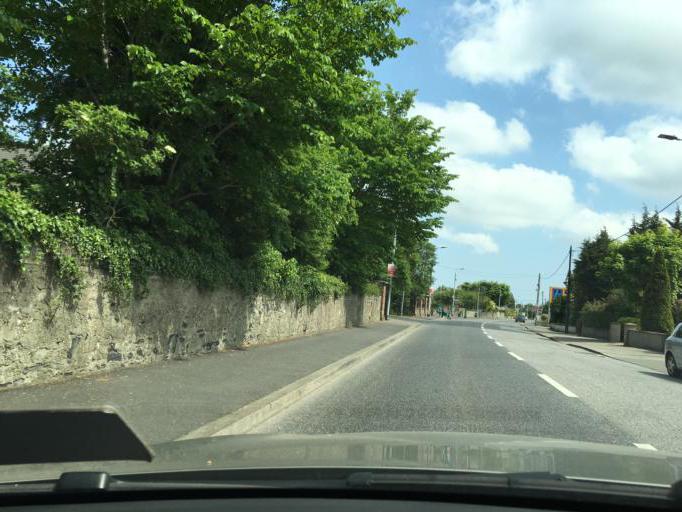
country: IE
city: Palmerstown
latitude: 53.3578
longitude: -6.3768
